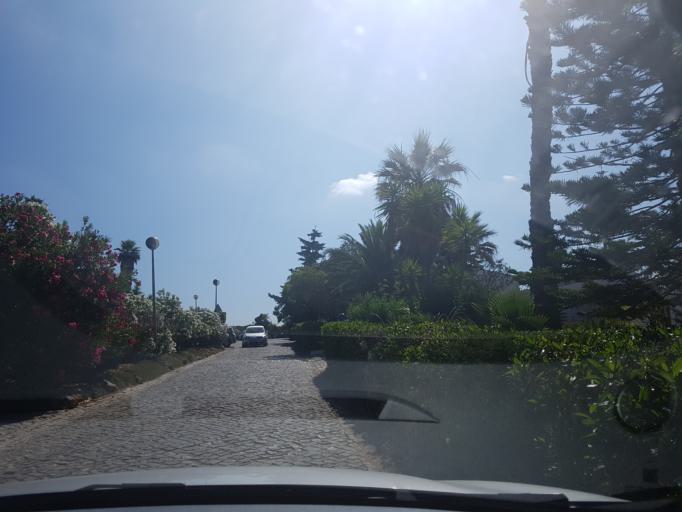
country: PT
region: Faro
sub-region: Lagoa
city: Carvoeiro
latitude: 37.0871
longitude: -8.4342
